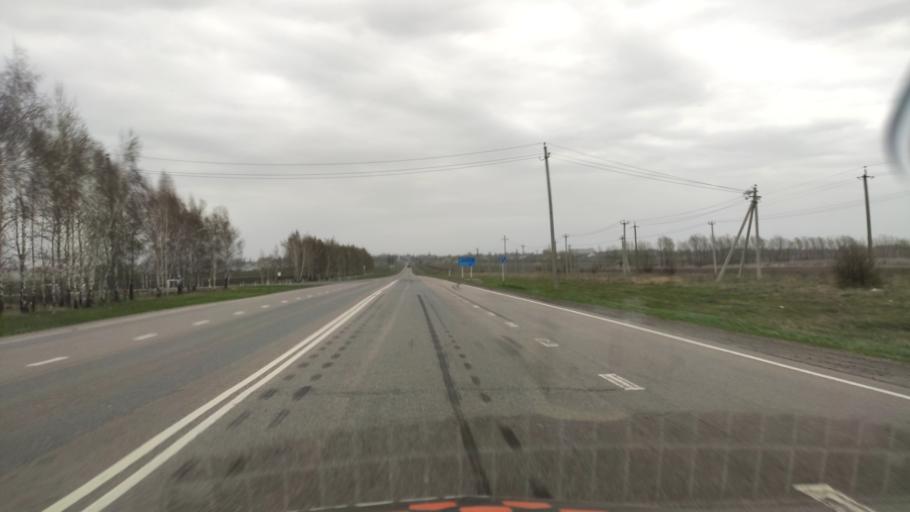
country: RU
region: Kursk
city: Gorshechnoye
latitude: 51.5063
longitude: 37.9947
